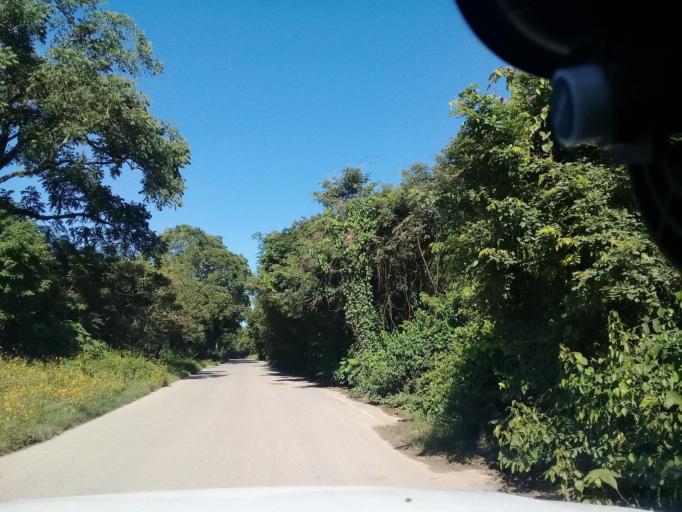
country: MX
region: Hidalgo
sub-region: Huejutla de Reyes
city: Huejutla de Reyes
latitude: 21.1650
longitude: -98.4194
